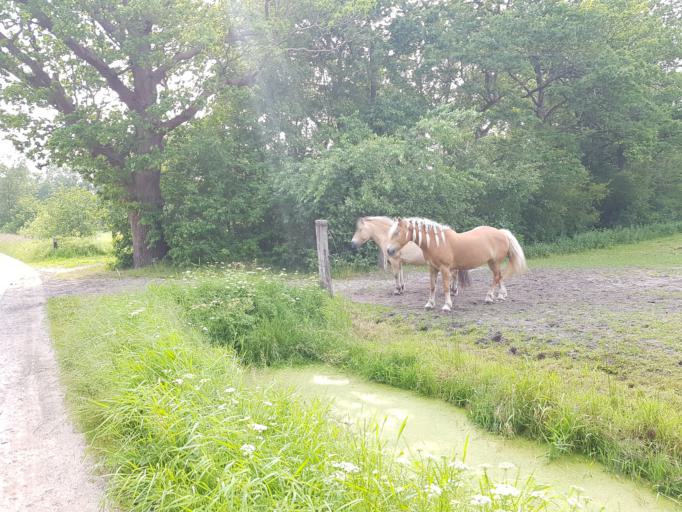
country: NL
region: Friesland
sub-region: Gemeente Heerenveen
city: Jubbega
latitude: 53.0321
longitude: 6.1096
